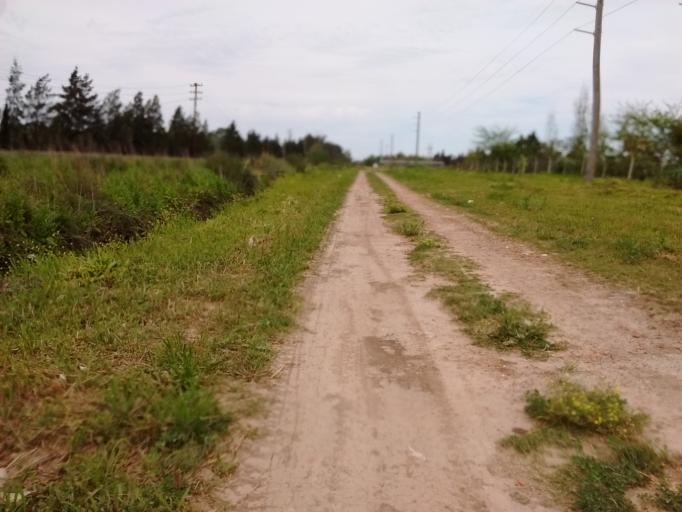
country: AR
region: Santa Fe
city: Funes
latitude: -32.9231
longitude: -60.7727
